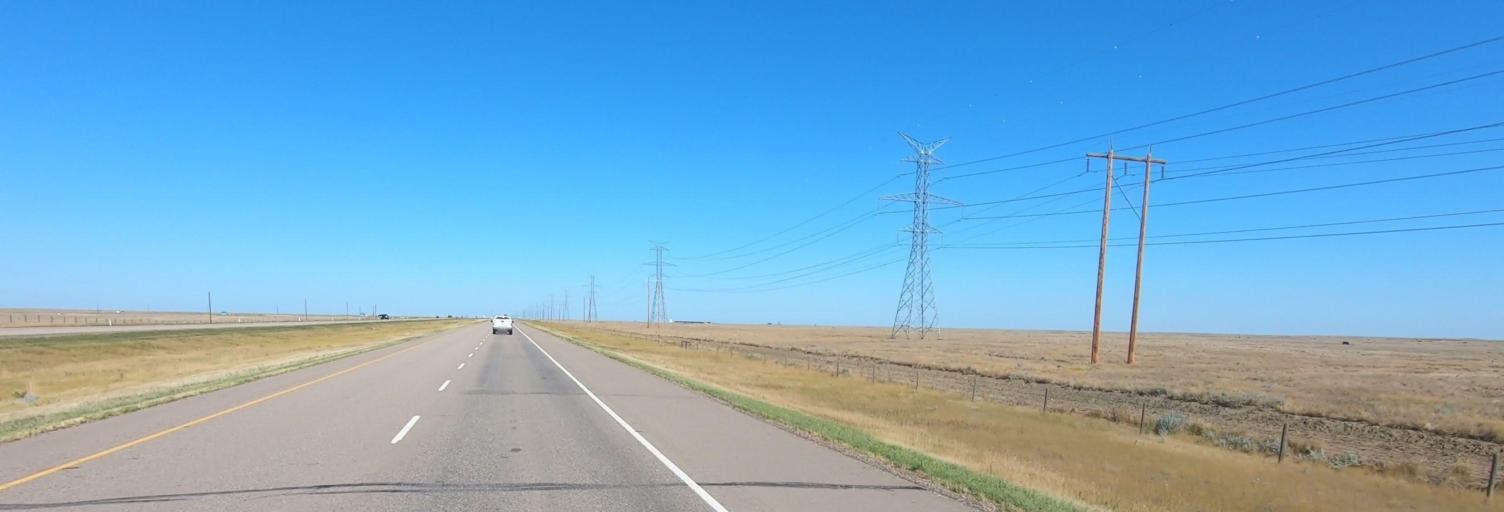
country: CA
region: Alberta
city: Brooks
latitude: 50.3947
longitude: -111.4765
